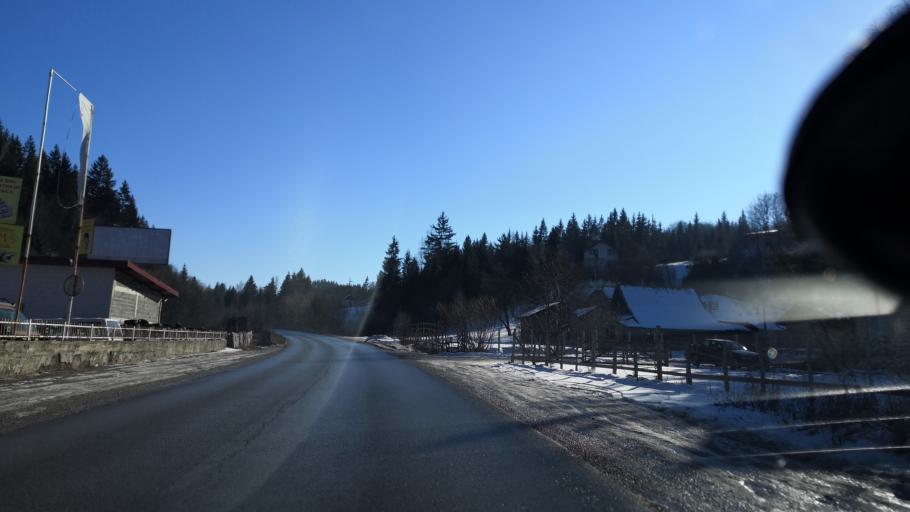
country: BA
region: Republika Srpska
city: Pale
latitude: 43.8420
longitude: 18.5520
